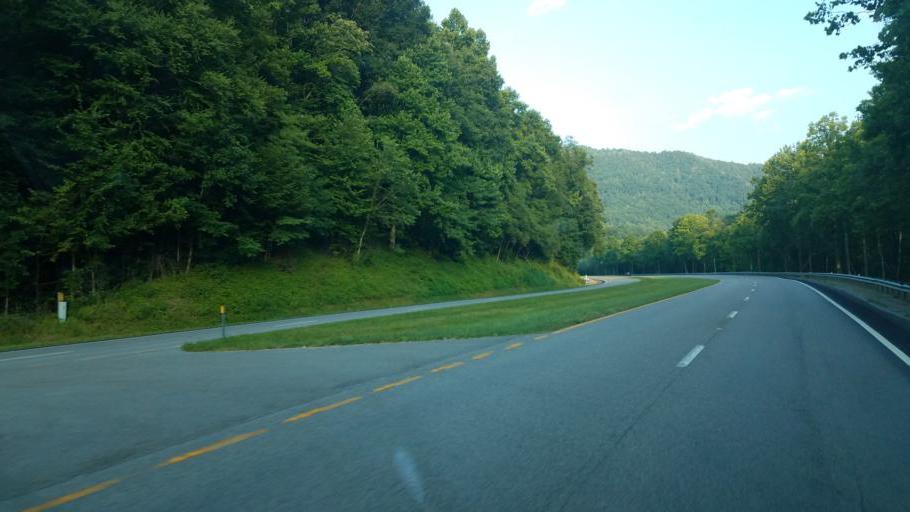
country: US
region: Virginia
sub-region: Lee County
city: Dryden
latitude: 36.7551
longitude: -82.8093
